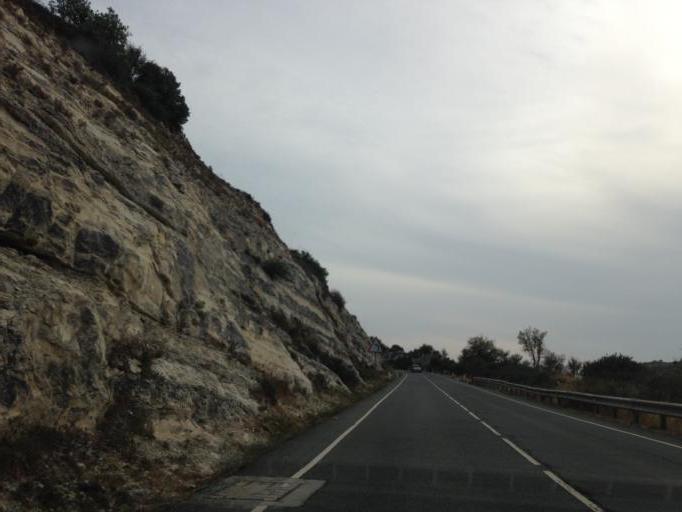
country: CY
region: Limassol
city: Pachna
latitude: 34.8059
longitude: 32.7910
